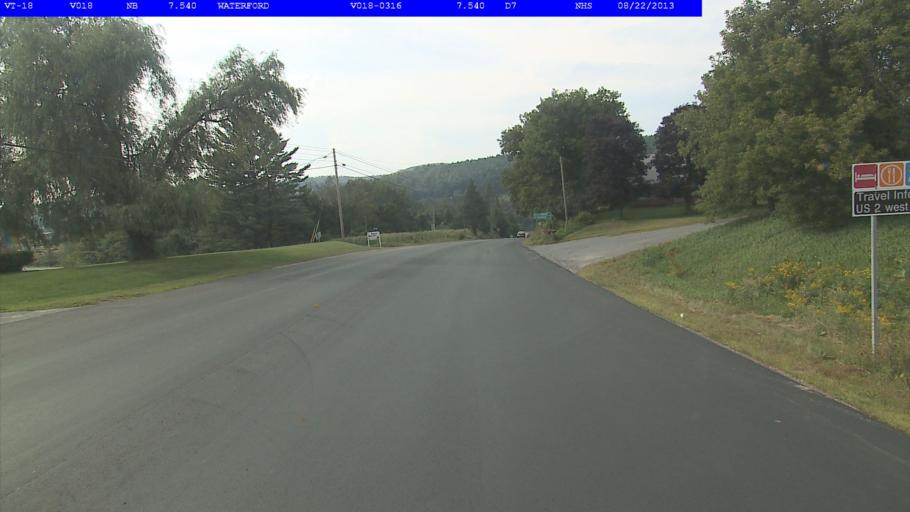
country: US
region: Vermont
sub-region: Caledonia County
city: St Johnsbury
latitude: 44.4267
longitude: -71.9581
